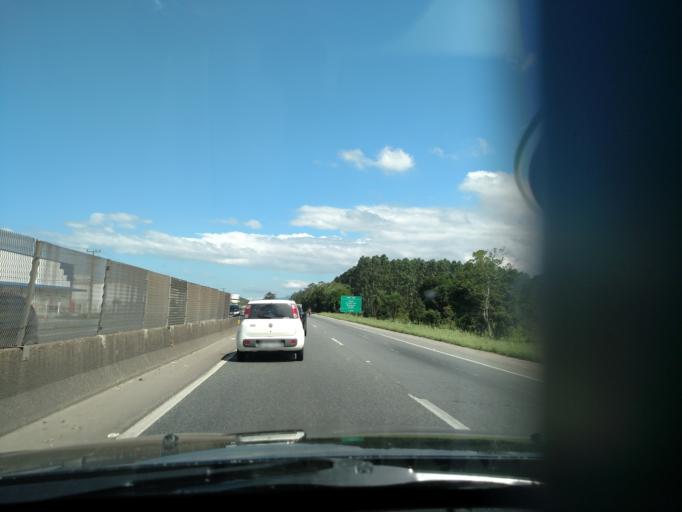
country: BR
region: Santa Catarina
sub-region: Itajai
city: Itajai
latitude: -26.9234
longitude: -48.7076
